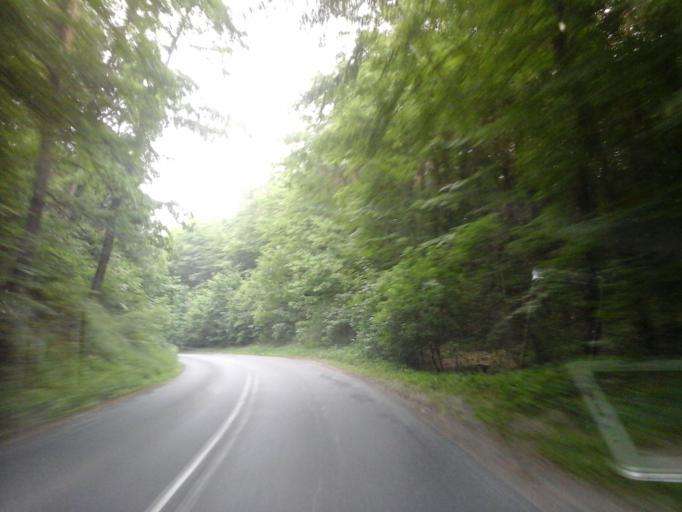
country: PL
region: West Pomeranian Voivodeship
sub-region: Powiat mysliborski
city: Barlinek
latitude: 52.9803
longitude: 15.2450
